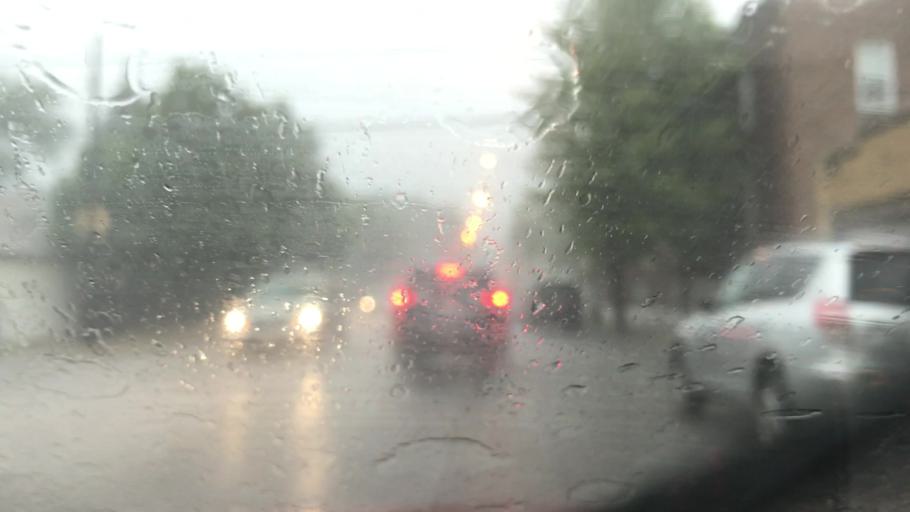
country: US
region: Illinois
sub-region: Cook County
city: Harwood Heights
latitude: 41.9499
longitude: -87.7570
